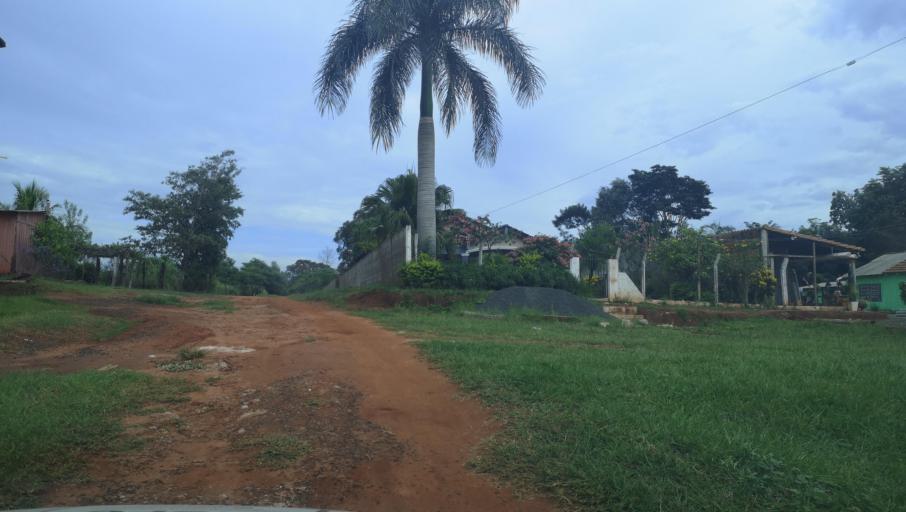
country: PY
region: San Pedro
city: Capiibary
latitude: -24.7435
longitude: -56.0261
